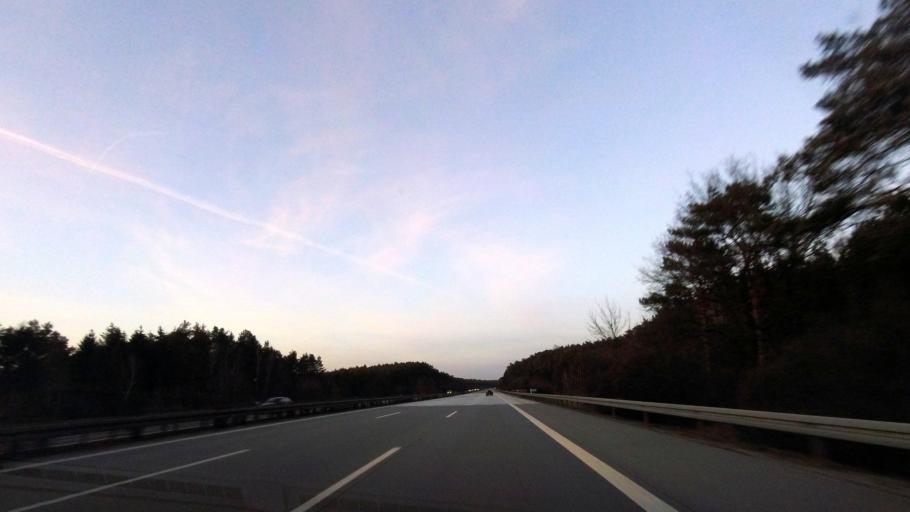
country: DE
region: Brandenburg
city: Erkner
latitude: 52.3513
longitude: 13.7586
